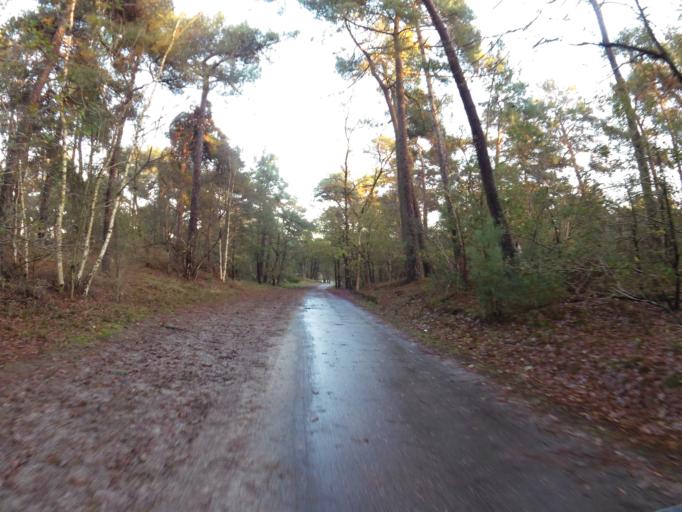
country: NL
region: North Brabant
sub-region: Gemeente Loon op Zand
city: Loon op Zand
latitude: 51.6374
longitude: 5.1055
